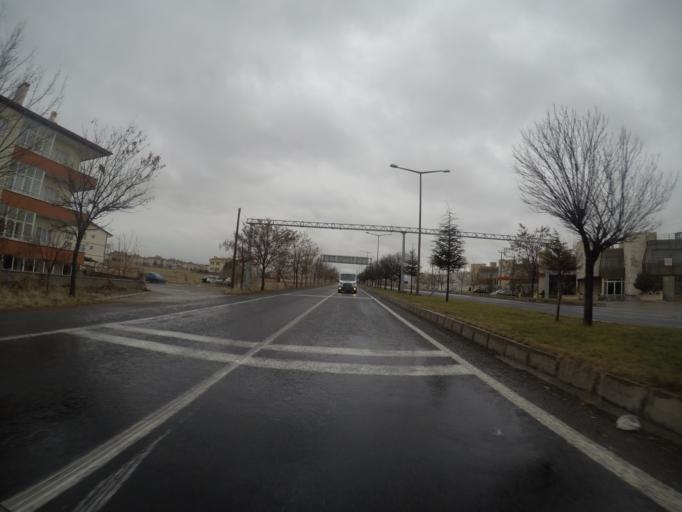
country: TR
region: Nevsehir
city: Avanos
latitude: 38.7042
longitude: 34.8561
